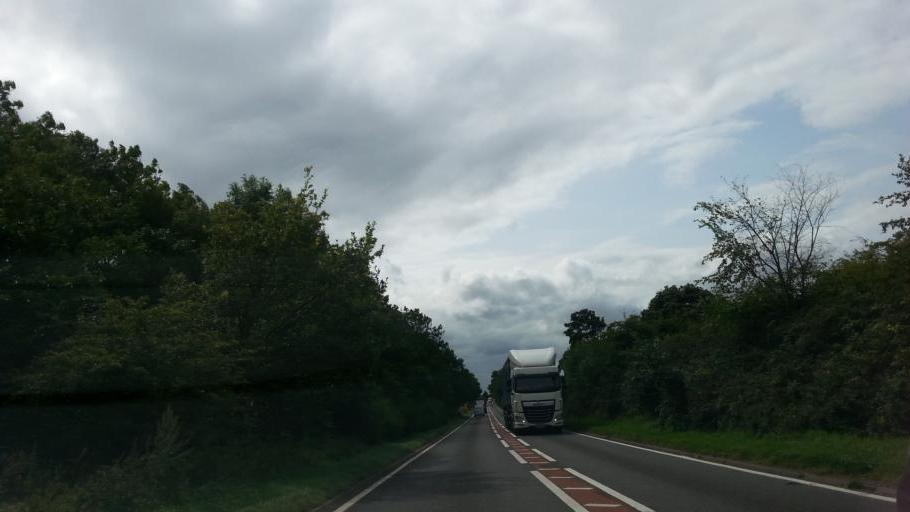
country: GB
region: England
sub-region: Northamptonshire
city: Earls Barton
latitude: 52.3070
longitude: -0.8183
